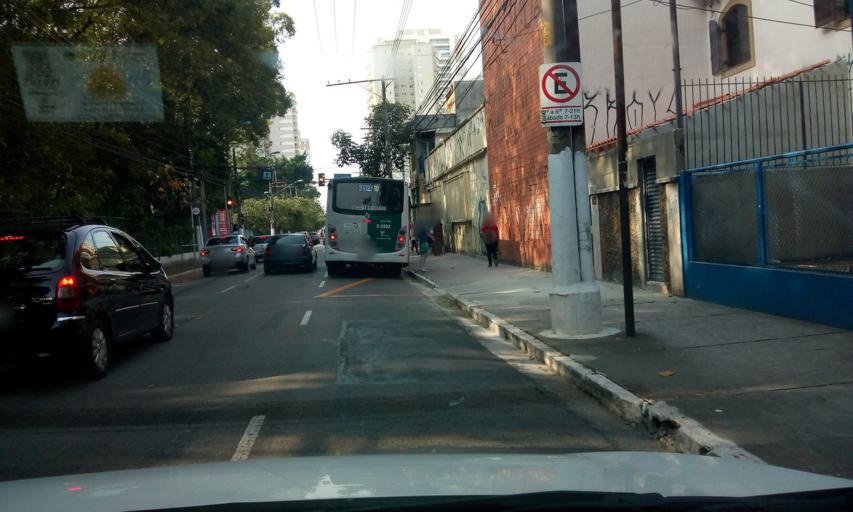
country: BR
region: Sao Paulo
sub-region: Sao Paulo
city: Sao Paulo
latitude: -23.5513
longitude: -46.5977
